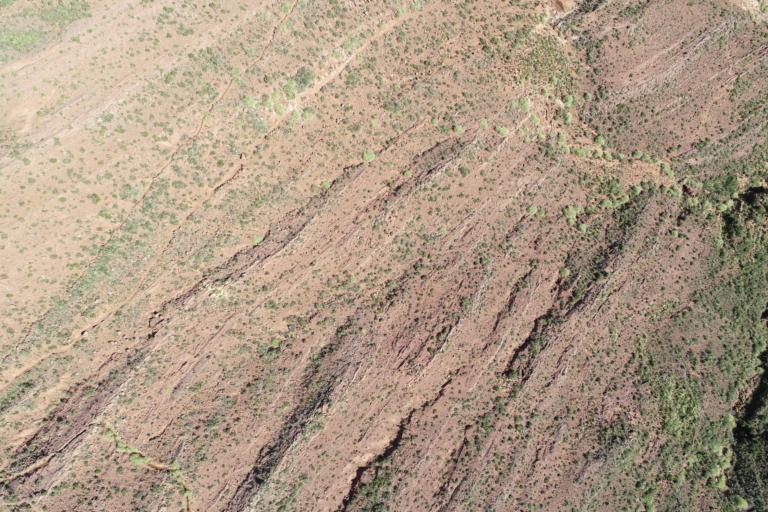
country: BO
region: La Paz
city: Tiahuanaco
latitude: -16.6055
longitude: -68.7584
